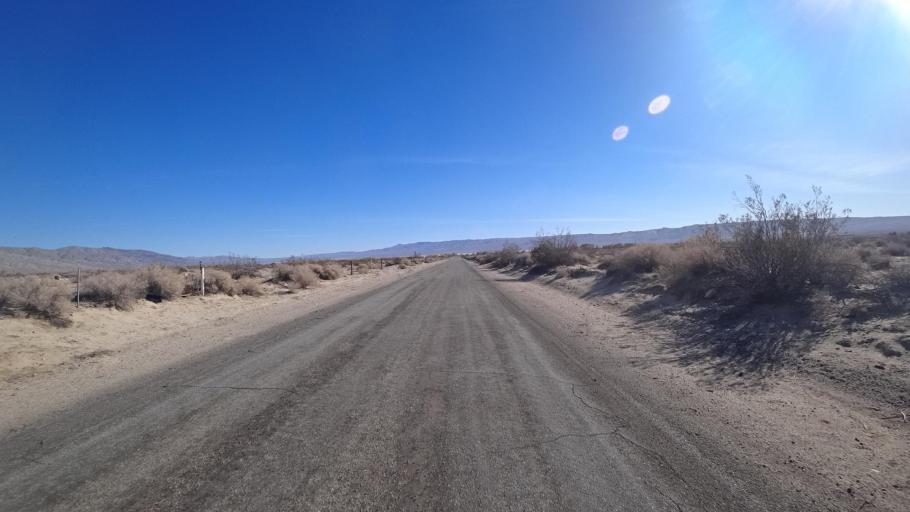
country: US
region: California
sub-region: Kern County
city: California City
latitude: 35.3162
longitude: -117.9451
